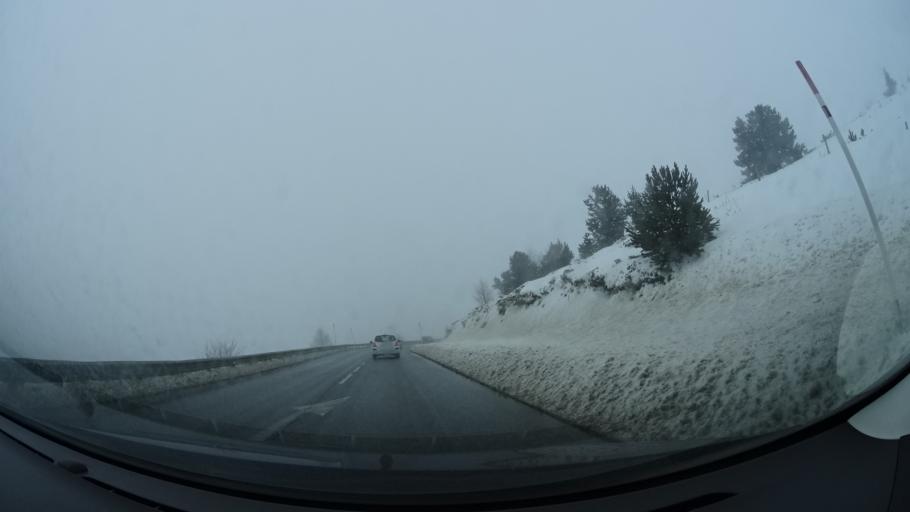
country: AD
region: Encamp
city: Pas de la Casa
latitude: 42.5625
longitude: 1.7791
